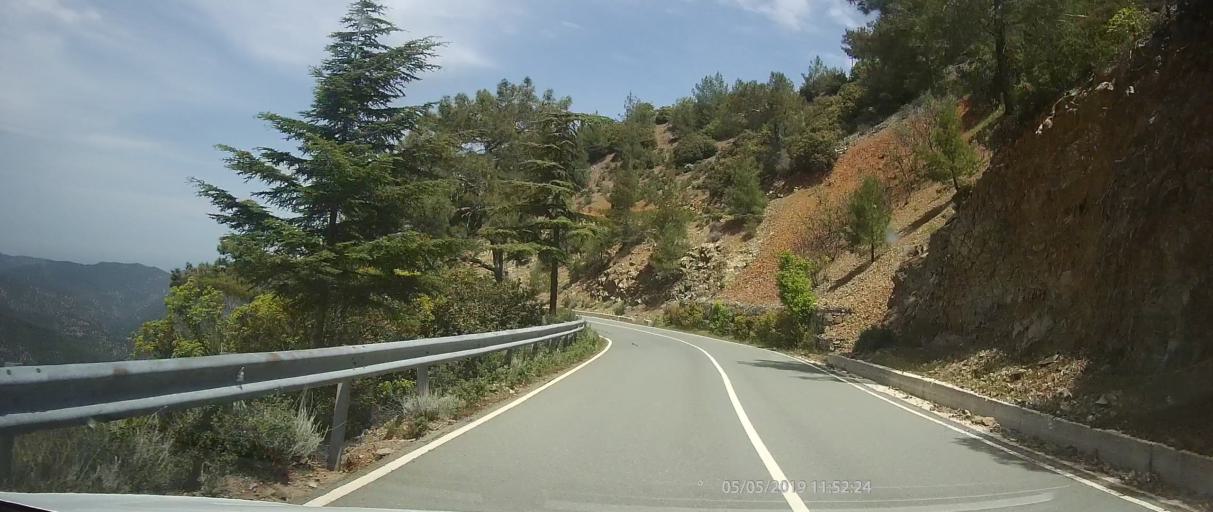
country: CY
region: Lefkosia
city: Kato Pyrgos
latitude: 35.0034
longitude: 32.7041
